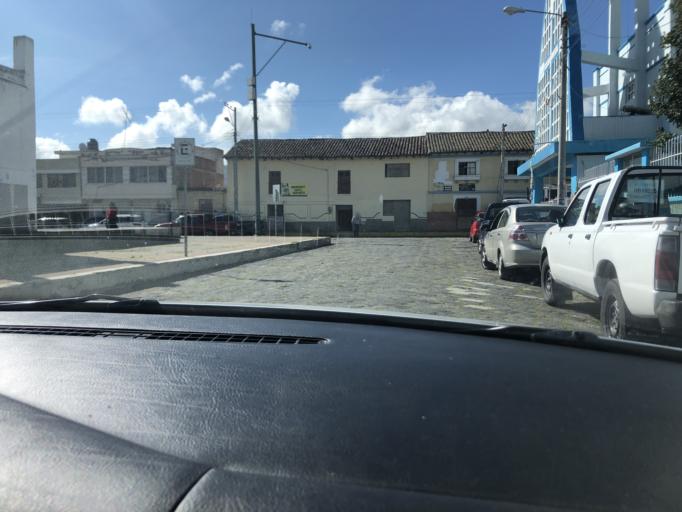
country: EC
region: Chimborazo
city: Riobamba
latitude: -1.7019
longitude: -78.7738
